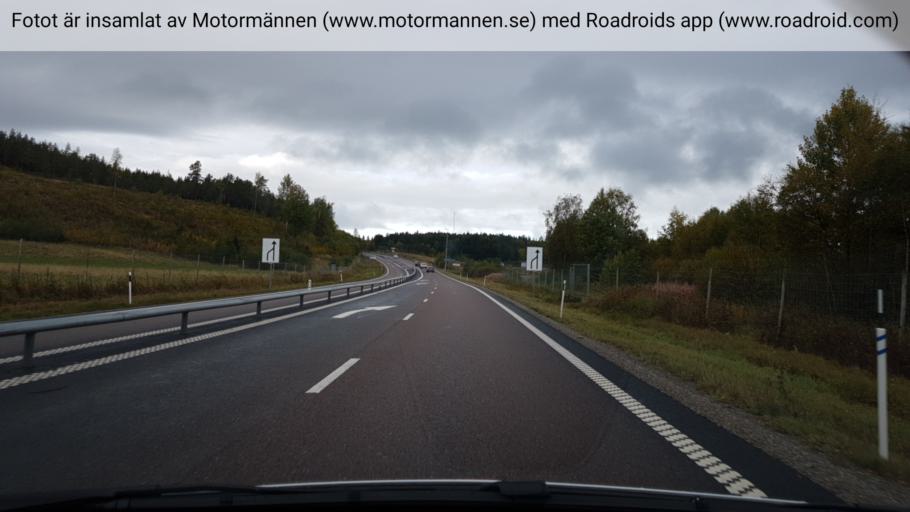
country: SE
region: Vaesternorrland
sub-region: OErnskoeldsviks Kommun
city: Ornskoldsvik
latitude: 63.3084
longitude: 18.8440
